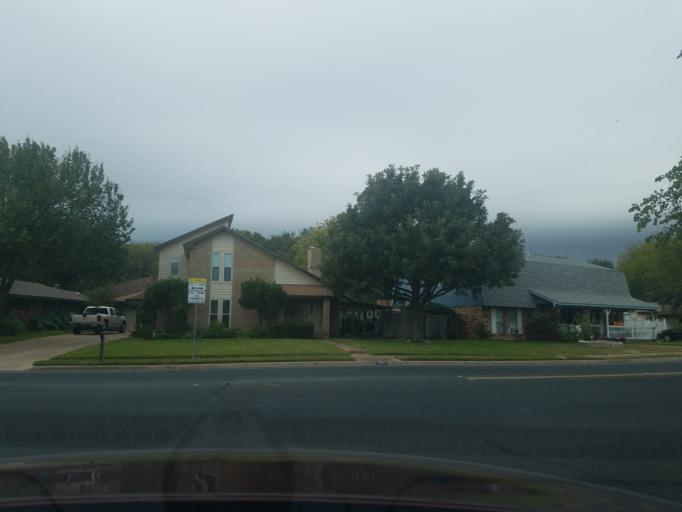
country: US
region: Texas
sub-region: Williamson County
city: Anderson Mill
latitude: 30.4590
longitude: -97.8074
